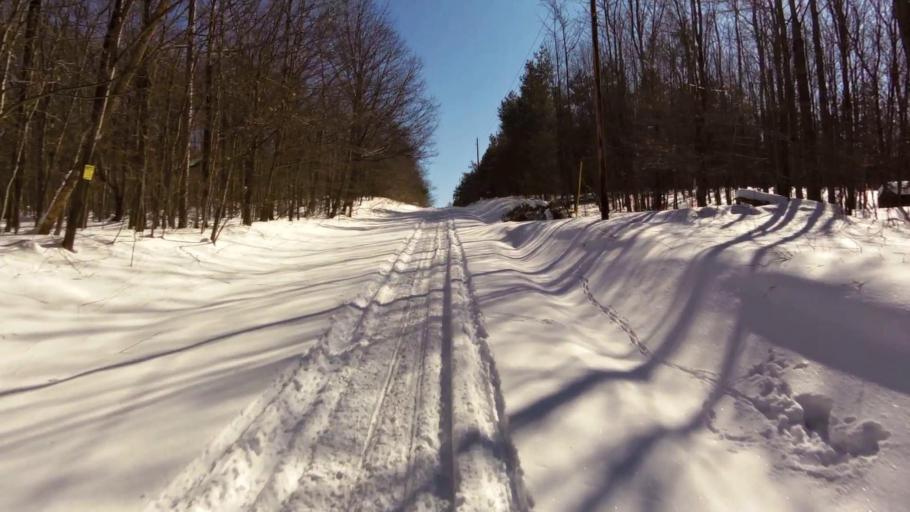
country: US
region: New York
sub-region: Allegany County
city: Cuba
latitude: 42.3313
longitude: -78.2908
